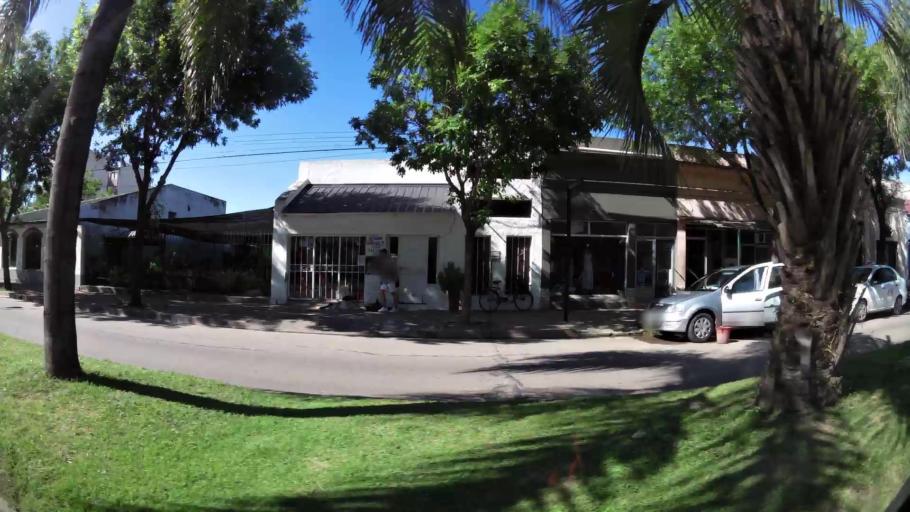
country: AR
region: Santa Fe
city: Esperanza
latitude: -31.4497
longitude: -60.9267
